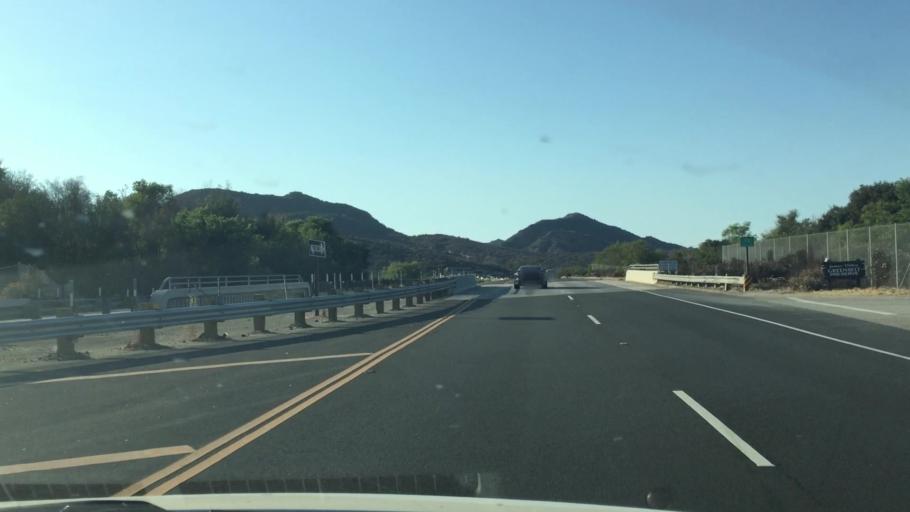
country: US
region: California
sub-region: Orange County
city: Laguna Woods
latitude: 33.5951
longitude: -117.7604
